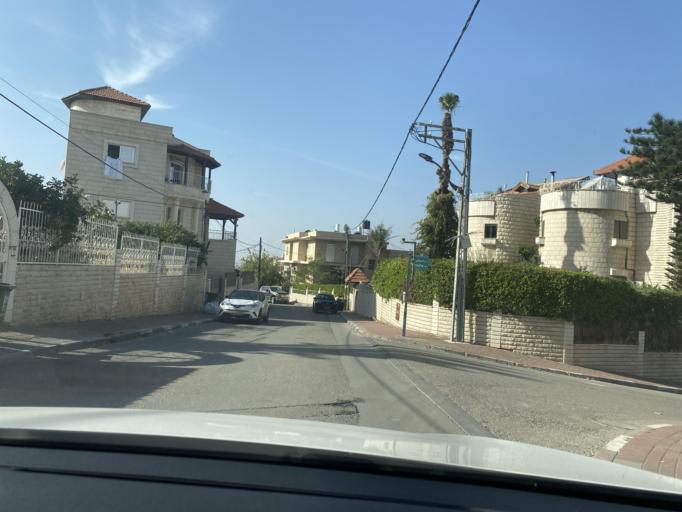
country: IL
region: Central District
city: Kafr Qasim
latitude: 32.1318
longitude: 34.9702
